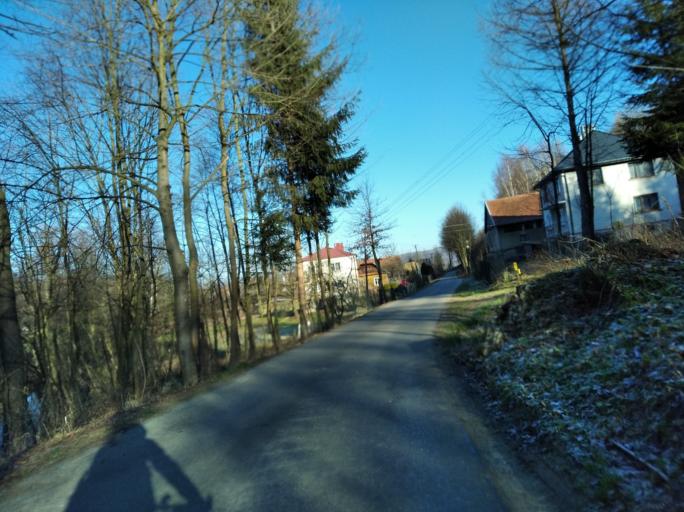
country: PL
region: Subcarpathian Voivodeship
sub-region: Powiat strzyzowski
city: Wysoka Strzyzowska
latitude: 49.8592
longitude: 21.7432
